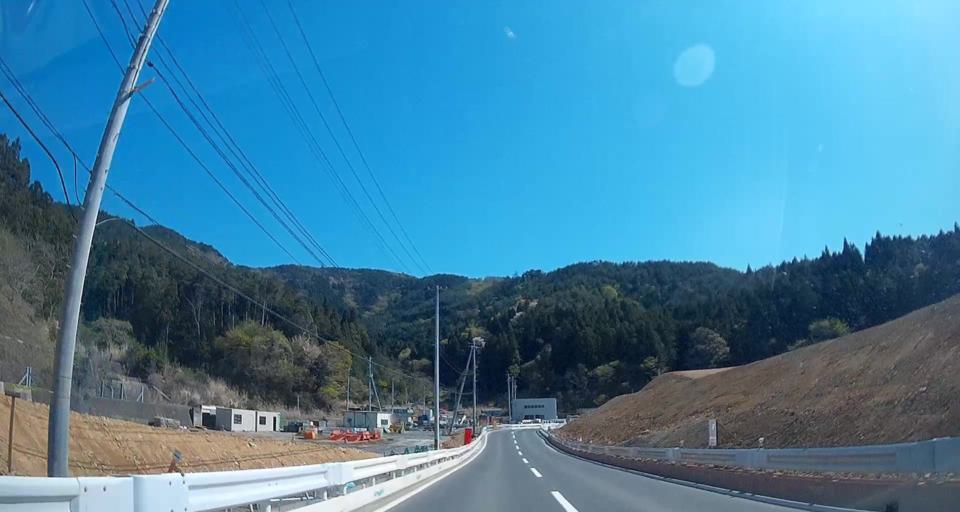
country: JP
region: Miyagi
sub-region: Oshika Gun
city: Onagawa Cho
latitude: 38.5221
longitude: 141.4693
